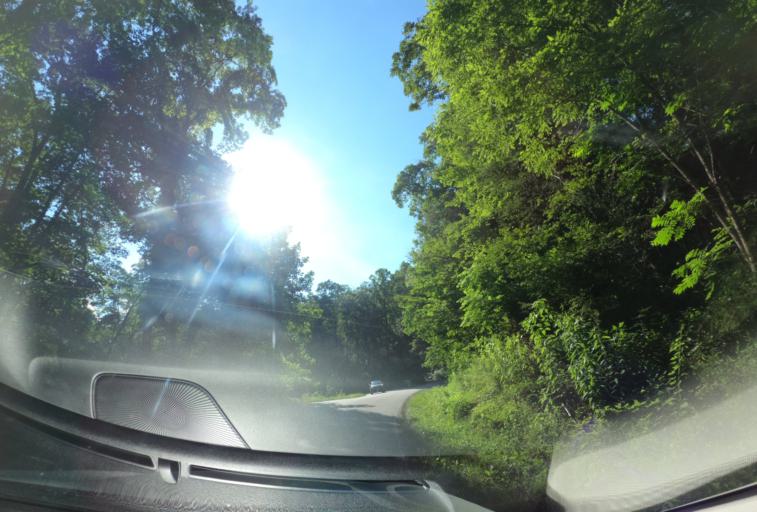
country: US
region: North Carolina
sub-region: Transylvania County
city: Brevard
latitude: 35.2853
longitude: -82.7934
